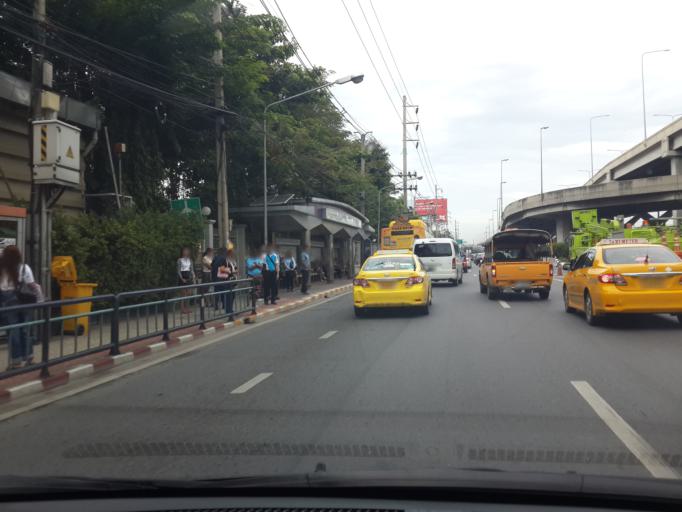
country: TH
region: Bangkok
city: Lak Si
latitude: 13.8969
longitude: 100.5891
